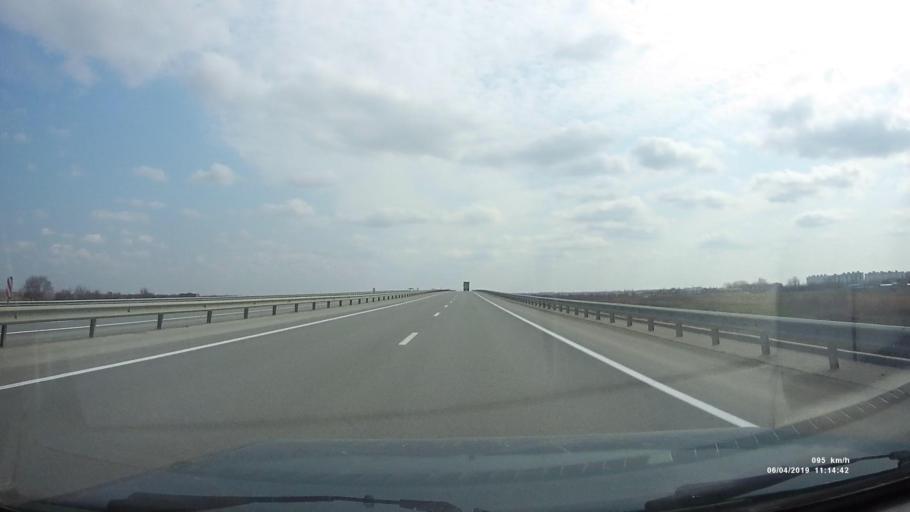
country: RU
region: Rostov
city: Kuleshovka
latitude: 47.0889
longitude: 39.5277
